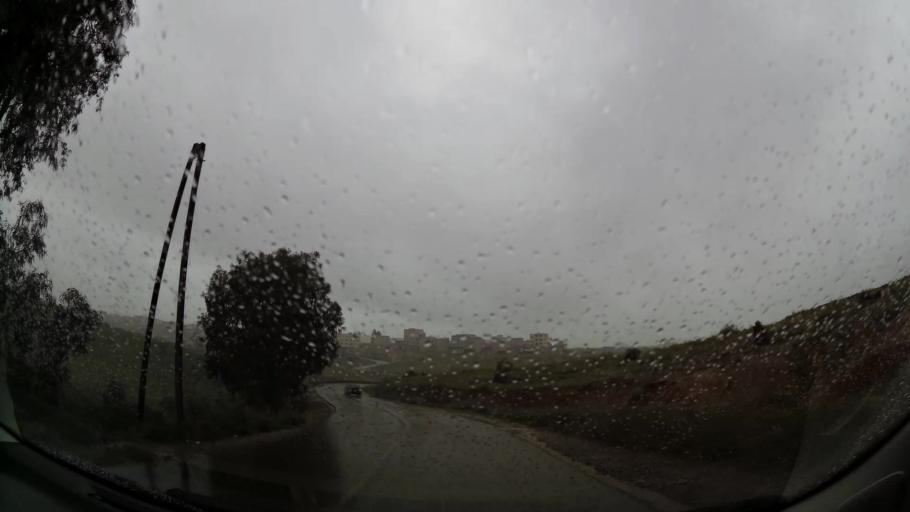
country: MA
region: Oriental
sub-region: Nador
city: Boudinar
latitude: 35.1227
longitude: -3.6336
